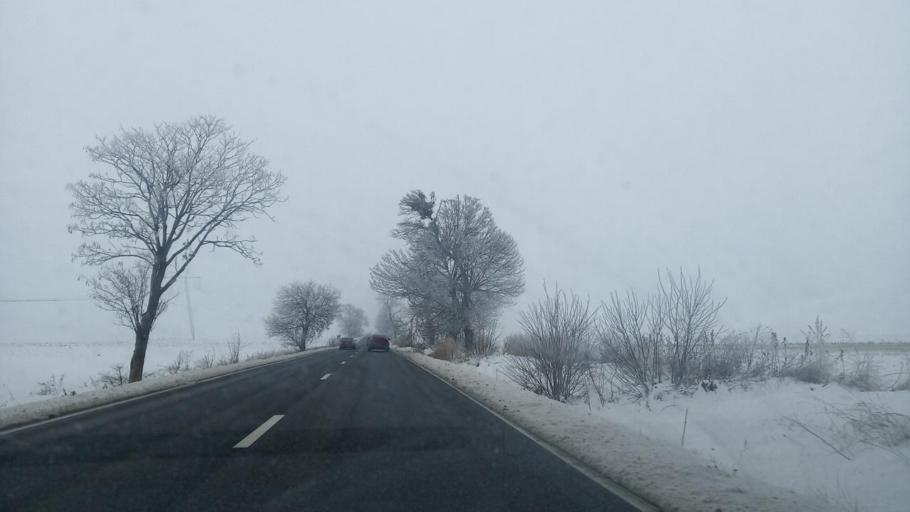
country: RO
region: Iasi
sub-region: Comuna Ciohorani
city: Ciohorani
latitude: 47.1058
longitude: 26.6901
